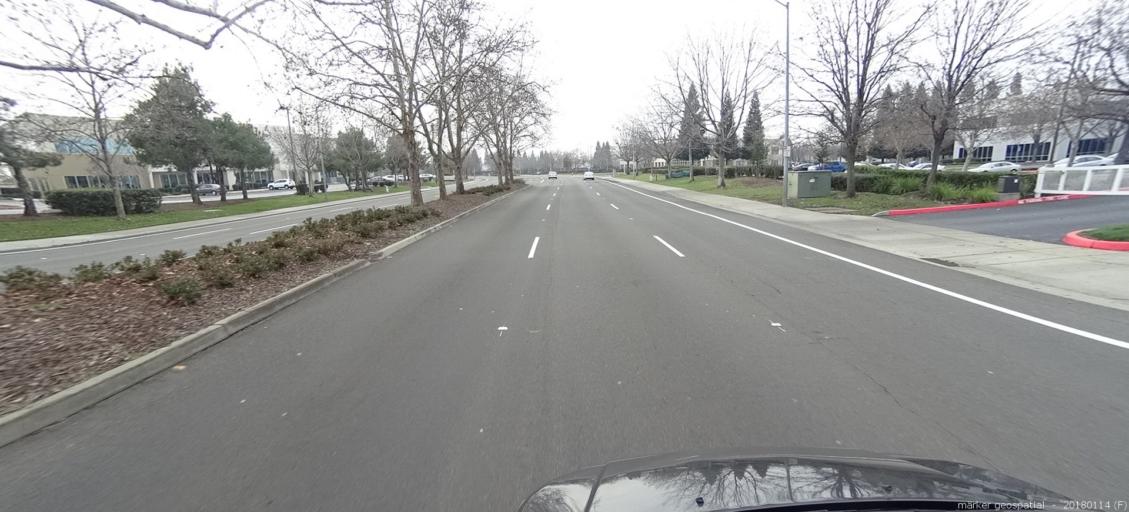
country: US
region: California
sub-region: Sacramento County
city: Rancho Cordova
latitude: 38.5812
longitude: -121.2860
